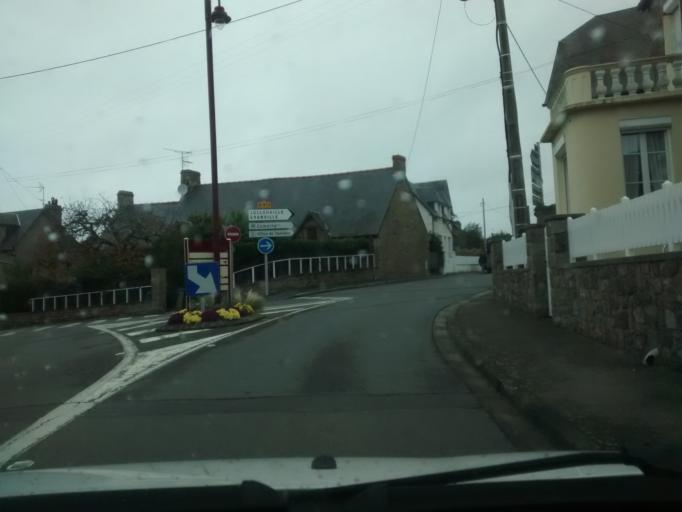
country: FR
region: Lower Normandy
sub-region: Departement de la Manche
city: Jullouville
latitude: 48.7485
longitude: -1.5587
